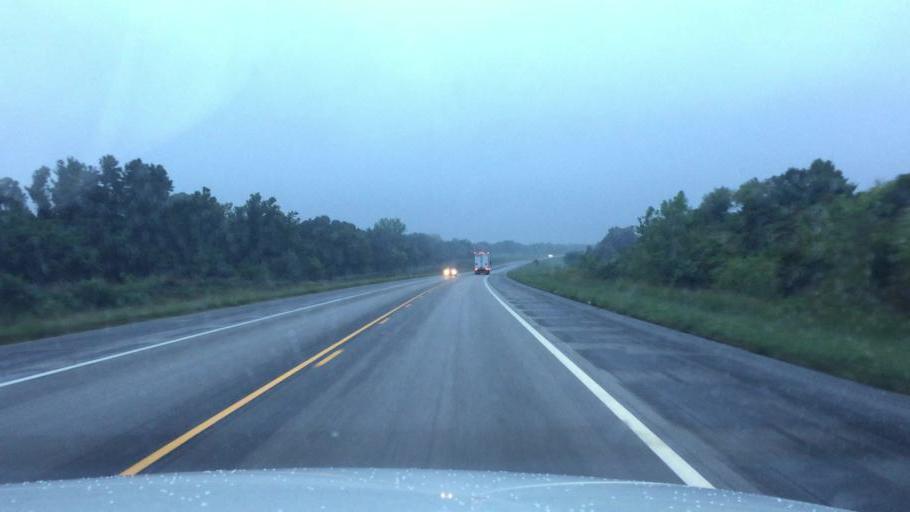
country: US
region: Kansas
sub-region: Montgomery County
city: Cherryvale
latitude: 37.4485
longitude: -95.4835
